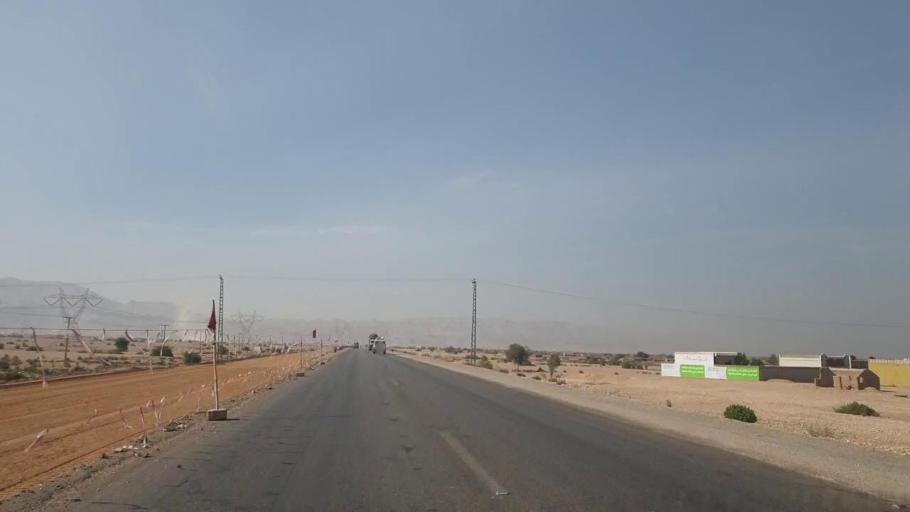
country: PK
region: Sindh
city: Sehwan
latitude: 26.2040
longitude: 67.9333
